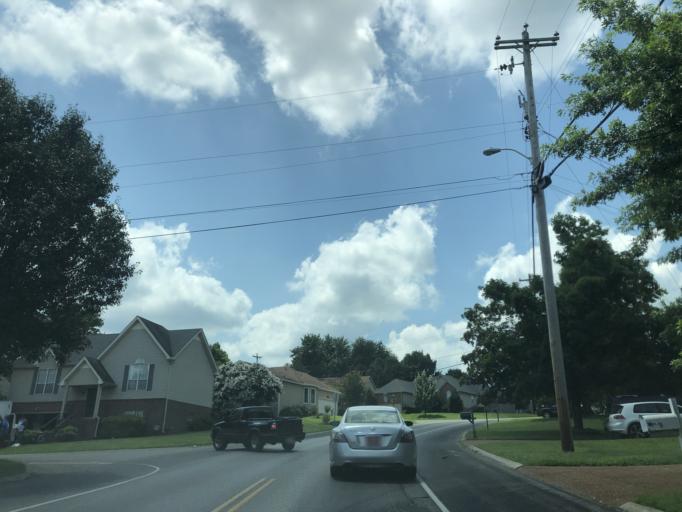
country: US
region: Tennessee
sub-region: Williamson County
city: Brentwood Estates
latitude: 36.0251
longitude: -86.7178
